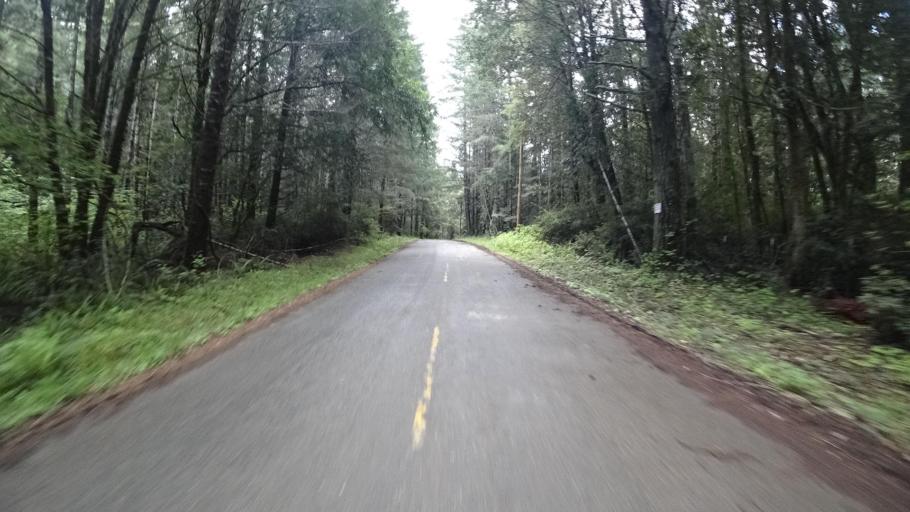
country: US
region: California
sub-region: Humboldt County
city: Blue Lake
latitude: 40.7629
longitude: -123.8814
